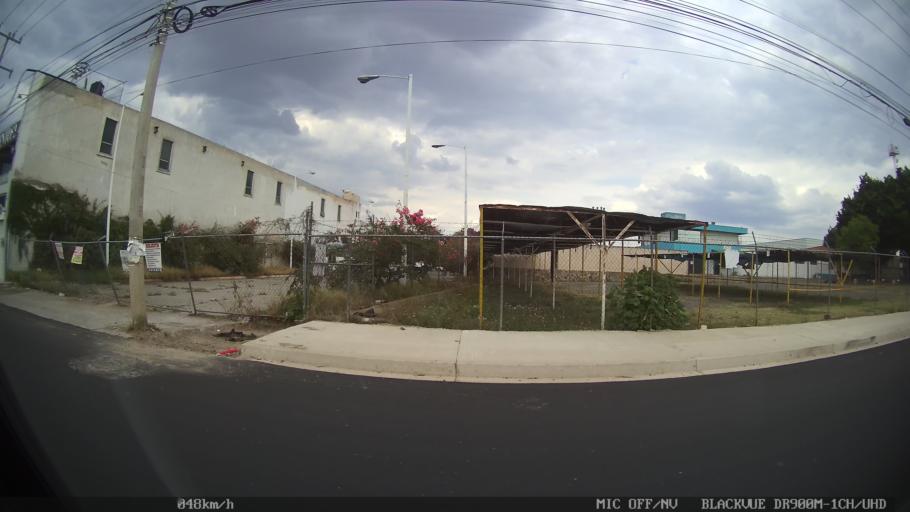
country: MX
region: Jalisco
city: Tlaquepaque
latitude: 20.6187
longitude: -103.2822
